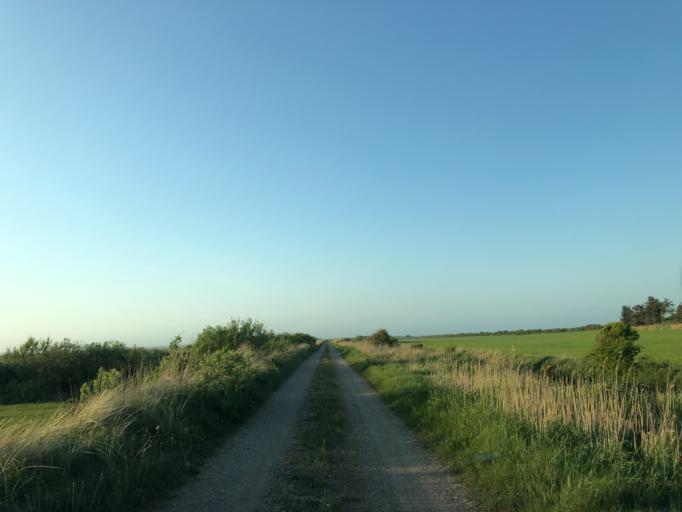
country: DK
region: Central Jutland
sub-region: Ringkobing-Skjern Kommune
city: Ringkobing
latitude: 56.2058
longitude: 8.1604
